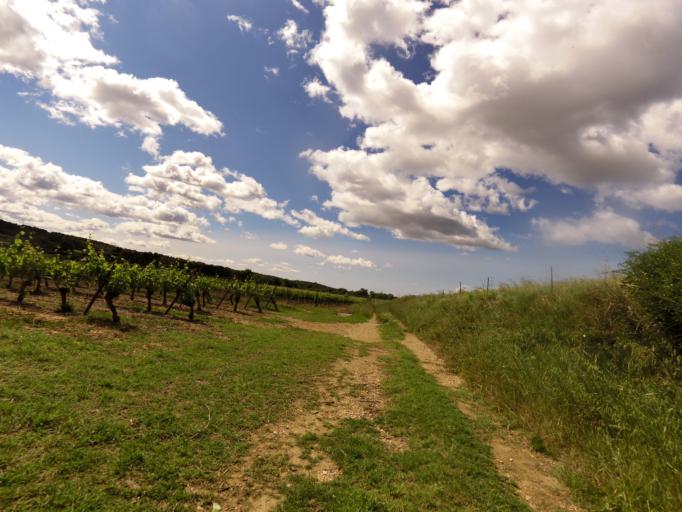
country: FR
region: Languedoc-Roussillon
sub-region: Departement du Gard
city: Calvisson
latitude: 43.7670
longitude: 4.2094
